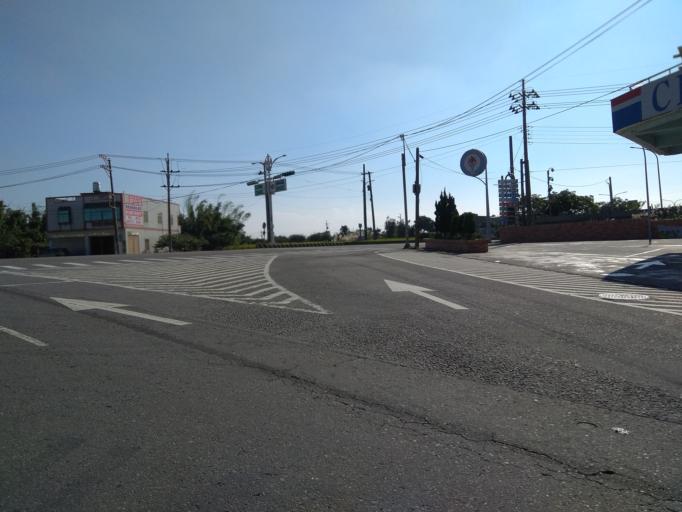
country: TW
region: Taiwan
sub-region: Hsinchu
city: Zhubei
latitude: 25.0255
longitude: 121.0866
